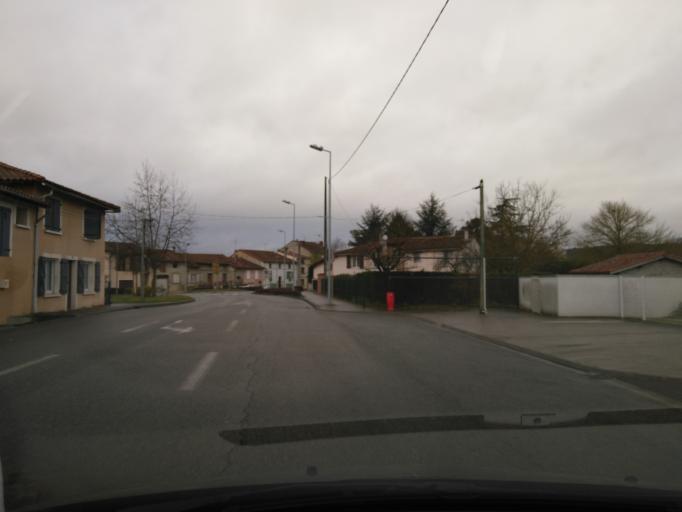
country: FR
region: Midi-Pyrenees
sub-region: Departement de la Haute-Garonne
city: Montesquieu-Volvestre
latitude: 43.2026
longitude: 1.2282
